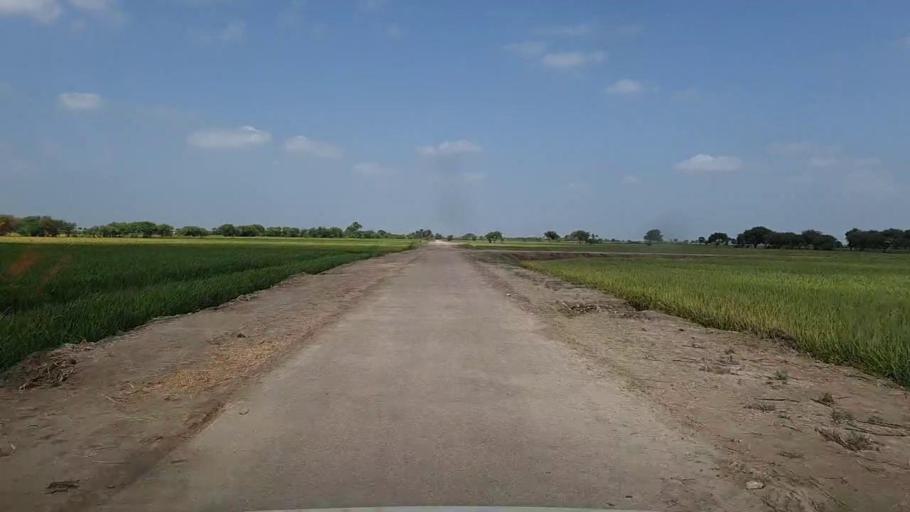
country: PK
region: Sindh
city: Kario
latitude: 24.6877
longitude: 68.5881
